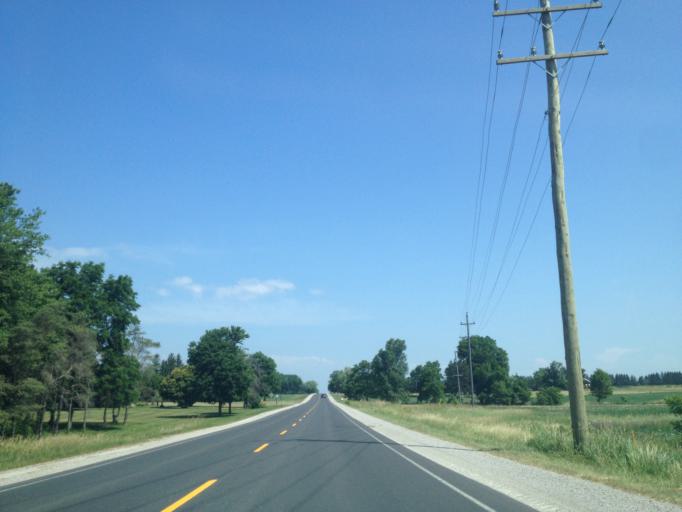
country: CA
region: Ontario
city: Stratford
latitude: 43.2721
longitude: -81.1938
